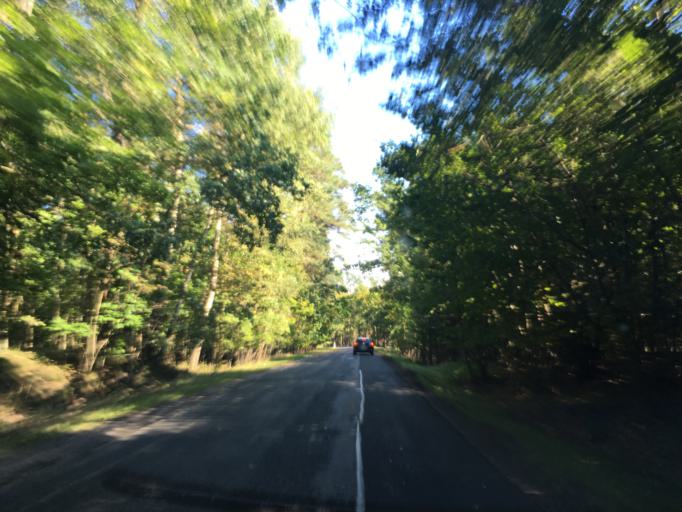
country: PL
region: Kujawsko-Pomorskie
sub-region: Powiat swiecki
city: Warlubie
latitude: 53.5961
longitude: 18.5855
